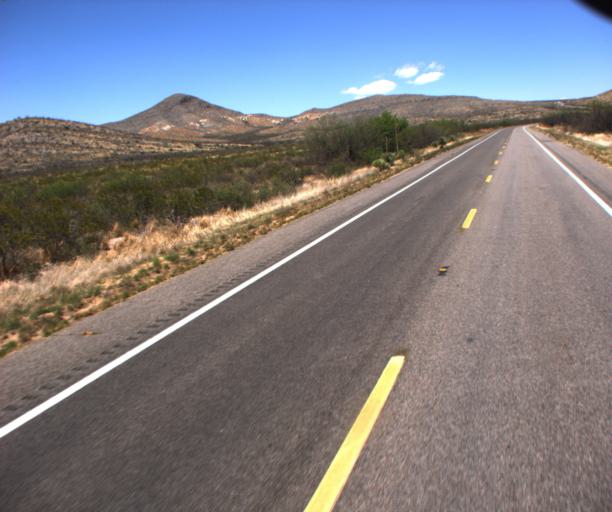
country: US
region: Arizona
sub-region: Cochise County
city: Tombstone
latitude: 31.6411
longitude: -110.0418
